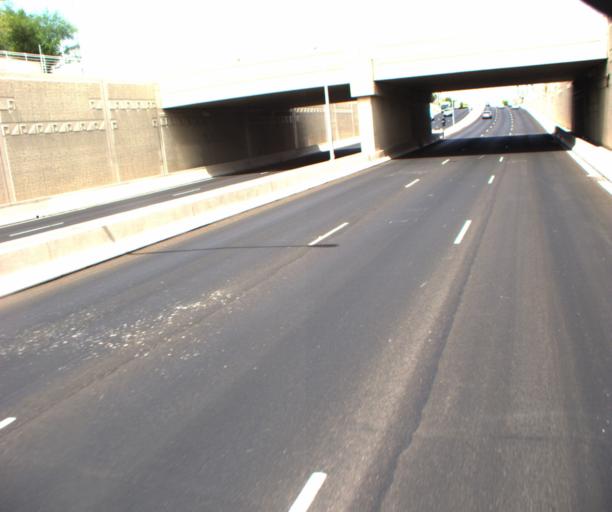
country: US
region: Arizona
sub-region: Maricopa County
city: Mesa
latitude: 33.4081
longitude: -111.8399
